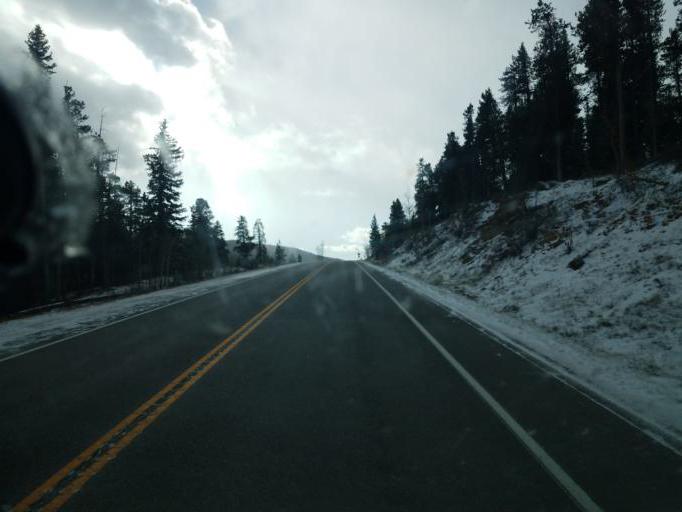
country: US
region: Colorado
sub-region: Summit County
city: Breckenridge
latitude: 39.4151
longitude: -105.7607
